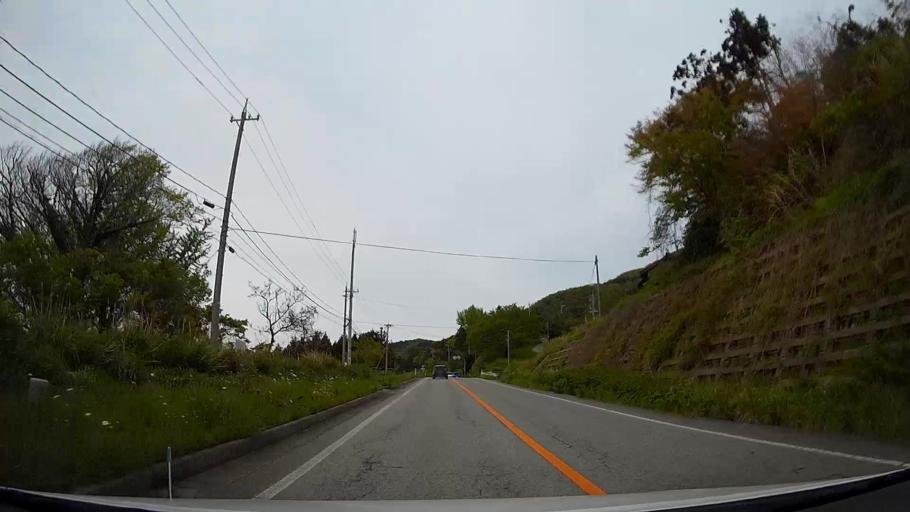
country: JP
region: Ishikawa
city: Nanao
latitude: 37.4219
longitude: 136.9919
